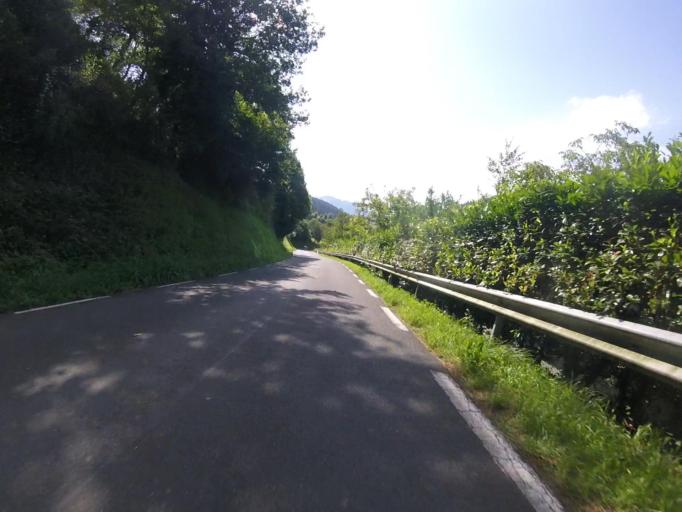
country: ES
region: Basque Country
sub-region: Provincia de Guipuzcoa
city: Alquiza
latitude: 43.1695
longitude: -2.1034
